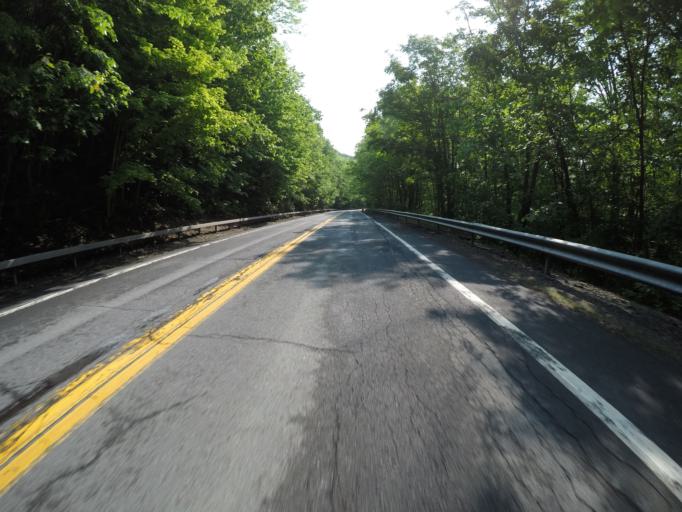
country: US
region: New York
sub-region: Sullivan County
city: Livingston Manor
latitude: 42.0895
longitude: -74.8103
